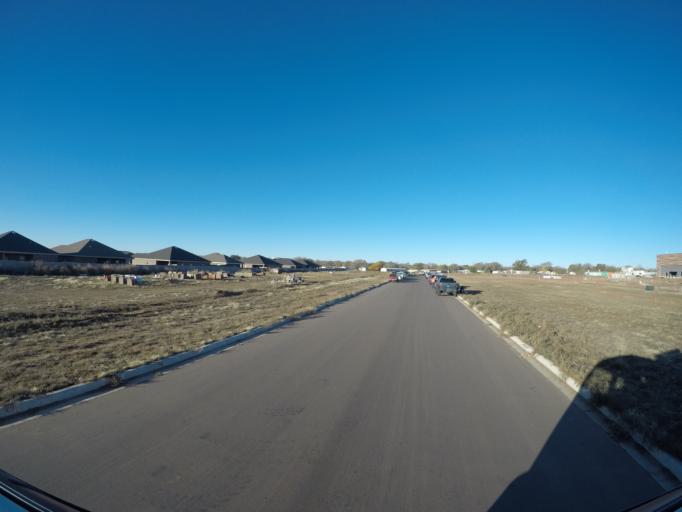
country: US
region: New Mexico
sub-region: Curry County
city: Clovis
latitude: 34.4097
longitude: -103.1717
